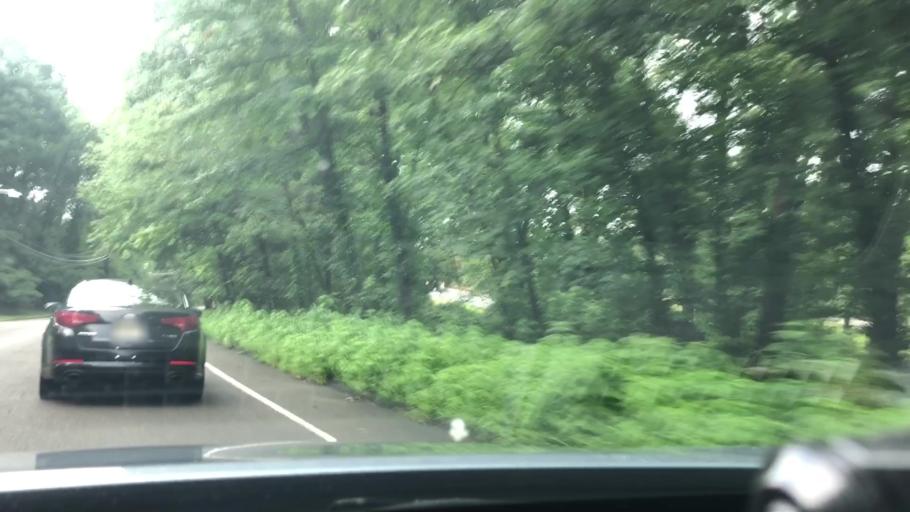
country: US
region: New Jersey
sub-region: Bergen County
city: Woodcliff Lake
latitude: 41.0229
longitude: -74.0706
